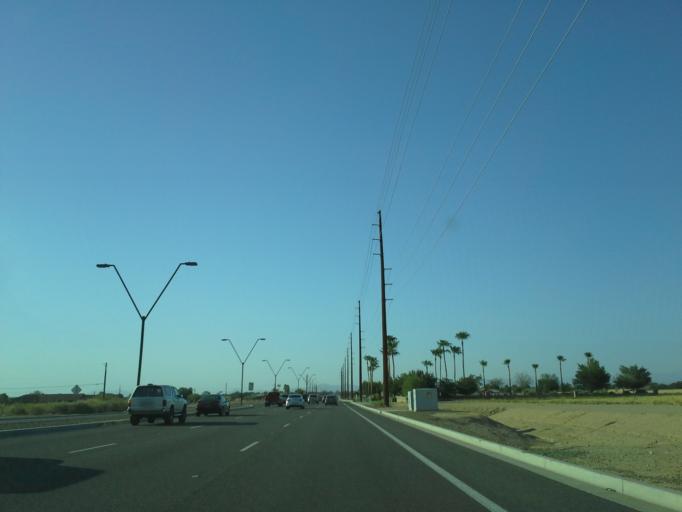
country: US
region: Arizona
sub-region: Maricopa County
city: Queen Creek
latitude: 33.2071
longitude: -111.6343
